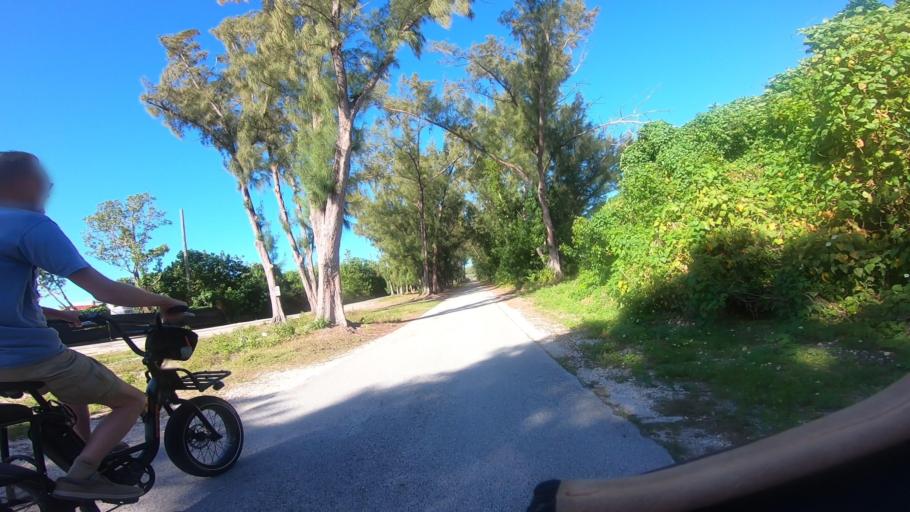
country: US
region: Florida
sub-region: Monroe County
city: Key Largo
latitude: 25.1118
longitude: -80.4277
